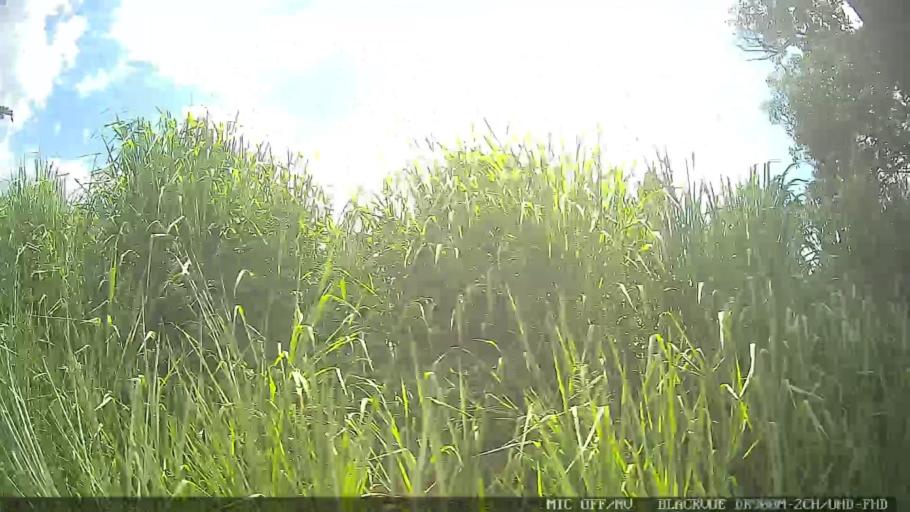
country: BR
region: Sao Paulo
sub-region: Atibaia
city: Atibaia
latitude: -23.1022
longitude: -46.6278
